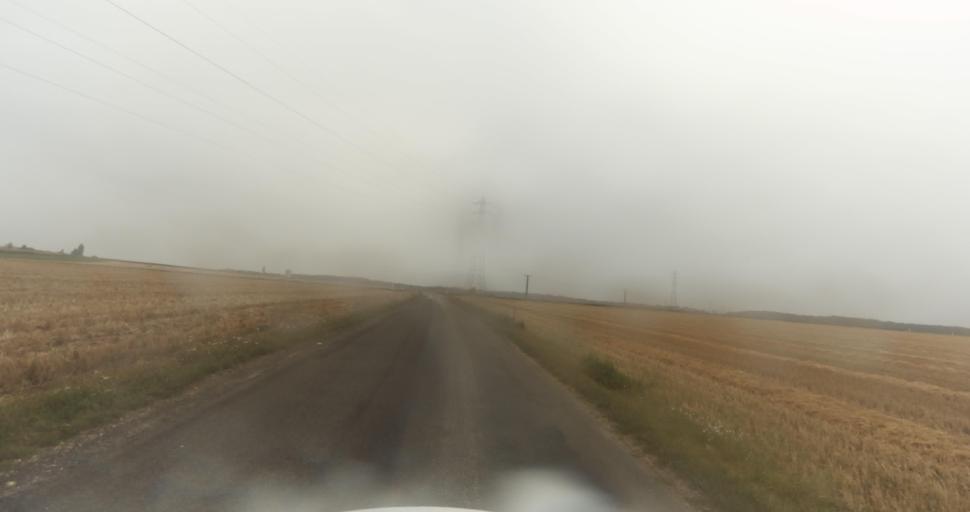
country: FR
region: Centre
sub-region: Departement d'Eure-et-Loir
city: Saint-Lubin-des-Joncherets
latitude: 48.7765
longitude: 1.2152
